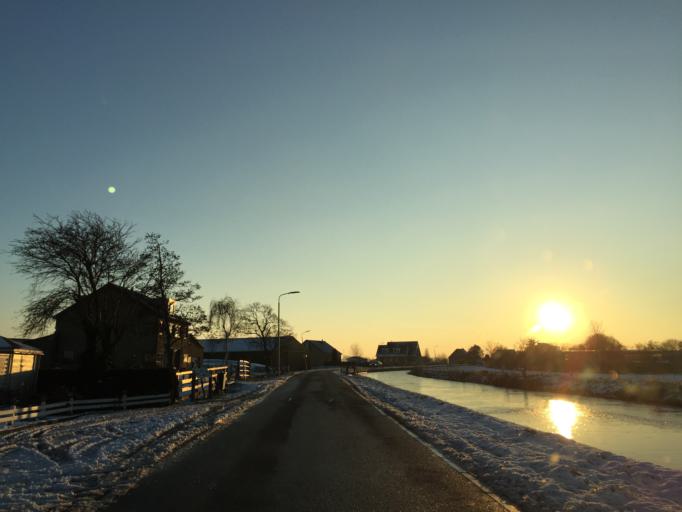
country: NL
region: South Holland
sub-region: Gemeente Pijnacker-Nootdorp
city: Pijnacker
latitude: 51.9946
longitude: 4.4403
